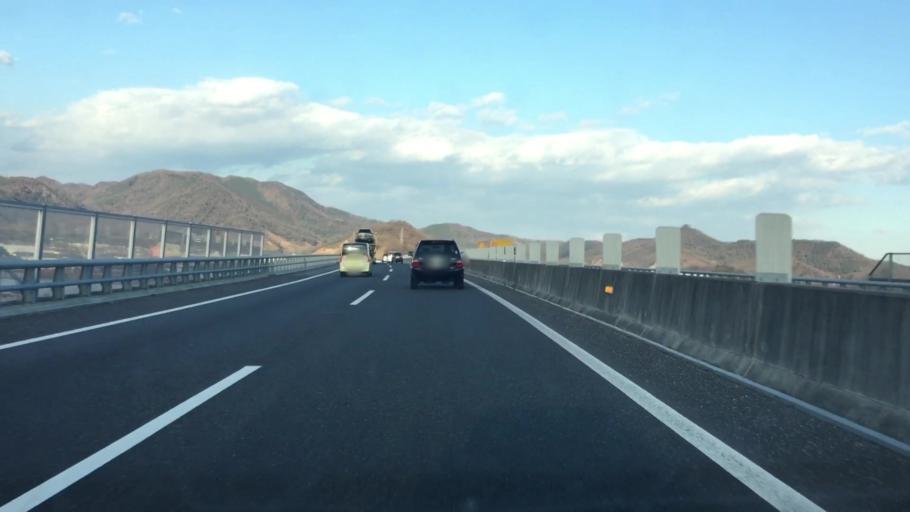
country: JP
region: Tochigi
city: Ashikaga
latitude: 36.3381
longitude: 139.4095
